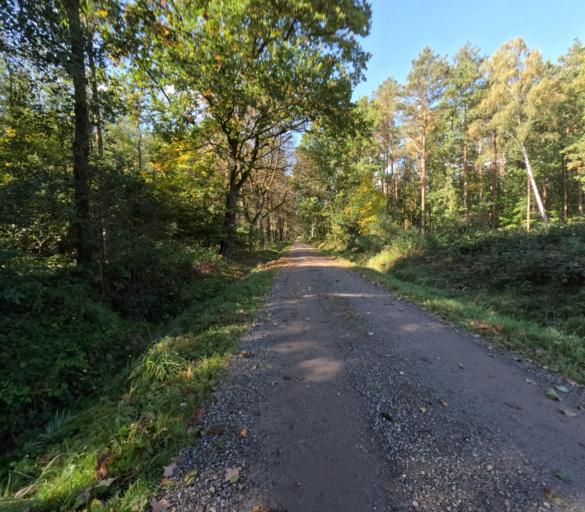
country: DE
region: Saxony
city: Moritzburg
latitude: 51.1694
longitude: 13.6626
